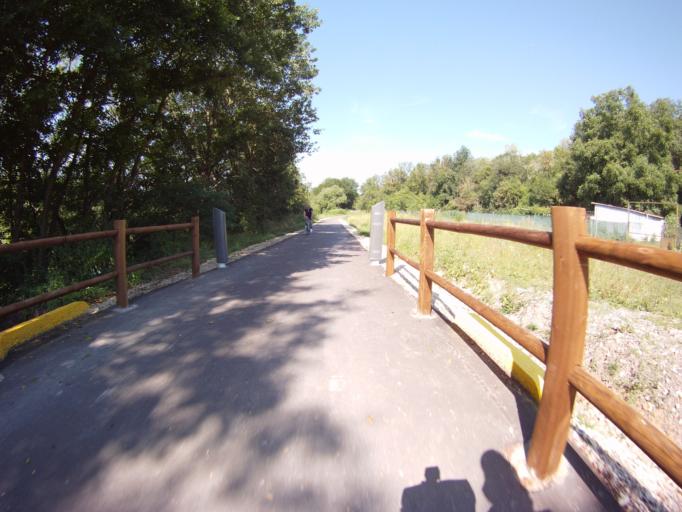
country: FR
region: Lorraine
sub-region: Departement de Meurthe-et-Moselle
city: Liverdun
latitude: 48.7581
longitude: 6.0523
